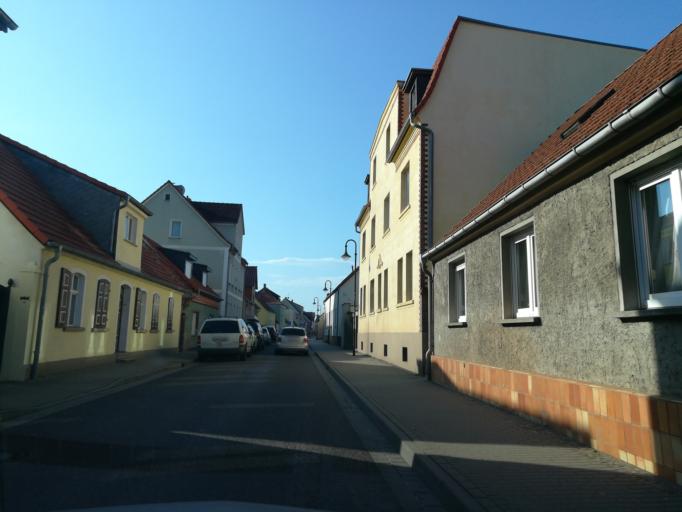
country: DE
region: Saxony-Anhalt
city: Gommern
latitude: 52.0704
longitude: 11.8211
